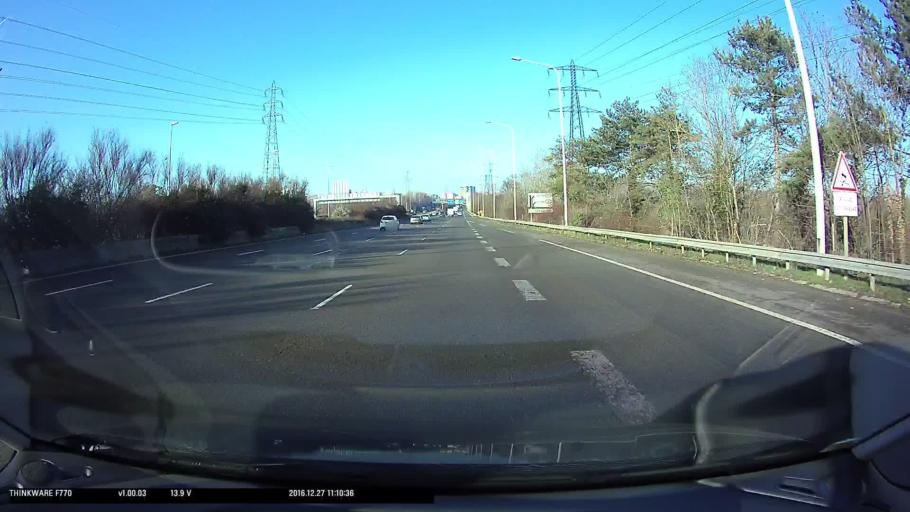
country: FR
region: Ile-de-France
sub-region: Departement du Val-d'Oise
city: Pontoise
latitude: 49.0348
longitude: 2.1009
